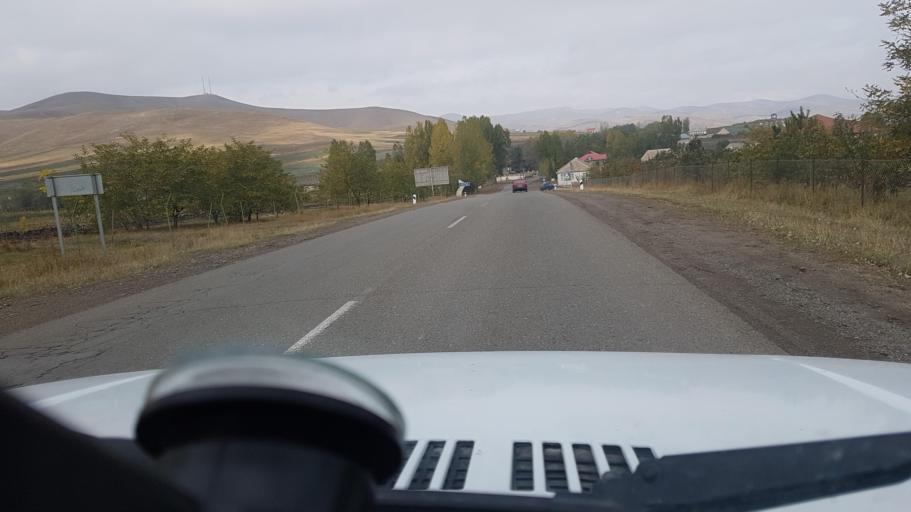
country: AZ
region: Gadabay Rayon
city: Ariqdam
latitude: 40.6312
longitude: 45.8141
